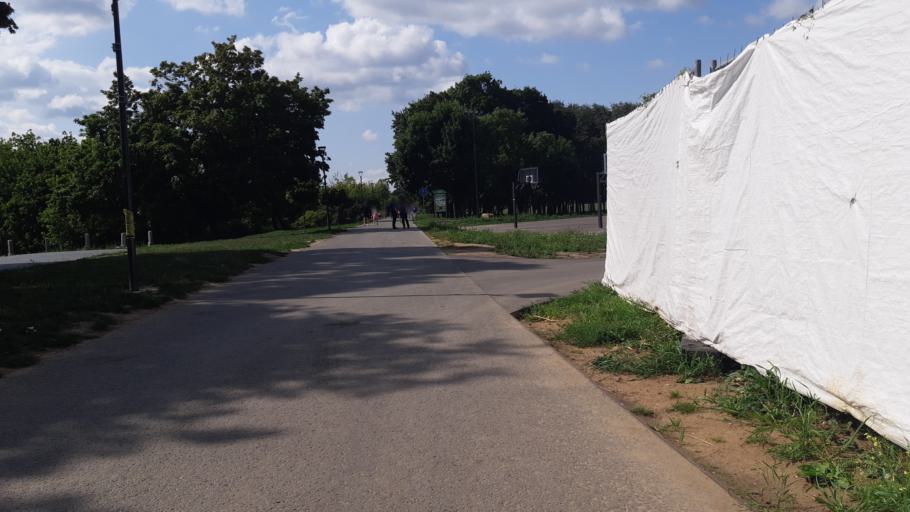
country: LT
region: Kauno apskritis
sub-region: Kaunas
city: Kaunas
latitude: 54.8956
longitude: 23.8821
